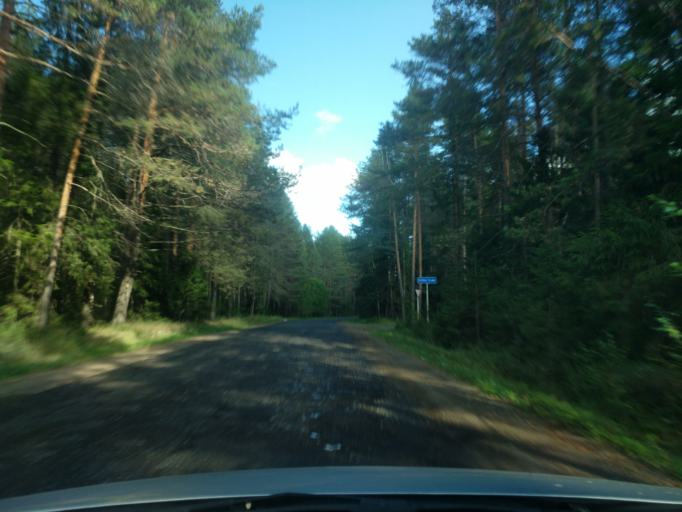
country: RU
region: Kirov
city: Kirovo-Chepetsk
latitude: 58.6054
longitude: 49.9186
